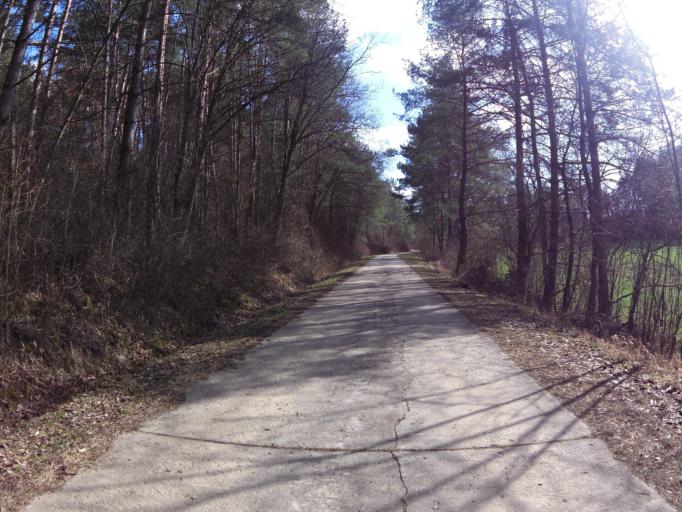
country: DE
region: Bavaria
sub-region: Regierungsbezirk Unterfranken
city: Hettstadt
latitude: 49.8363
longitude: 9.8117
